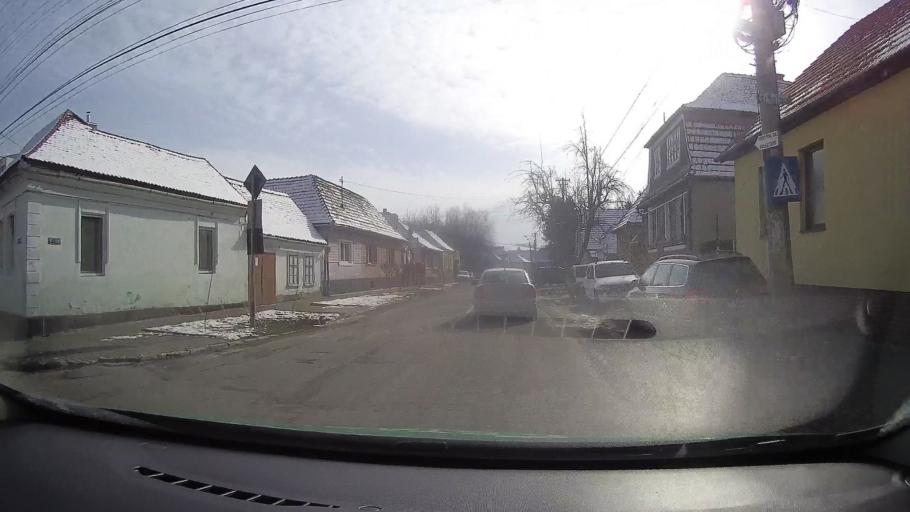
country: RO
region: Mures
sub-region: Municipiul Sighisoara
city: Sighisoara
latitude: 46.2150
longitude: 24.7826
